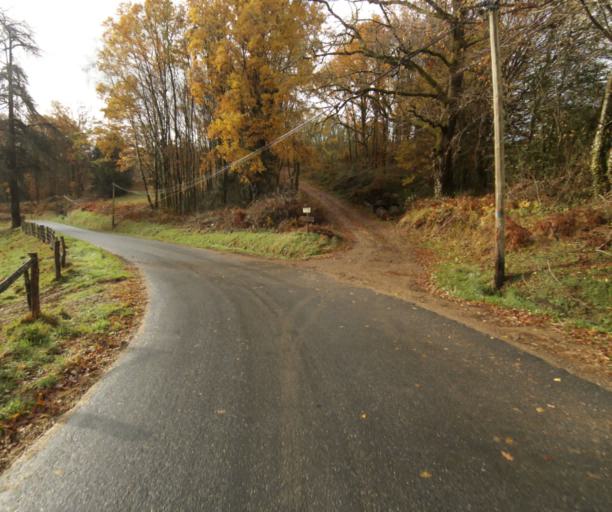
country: FR
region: Limousin
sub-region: Departement de la Correze
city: Cornil
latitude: 45.2043
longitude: 1.6512
